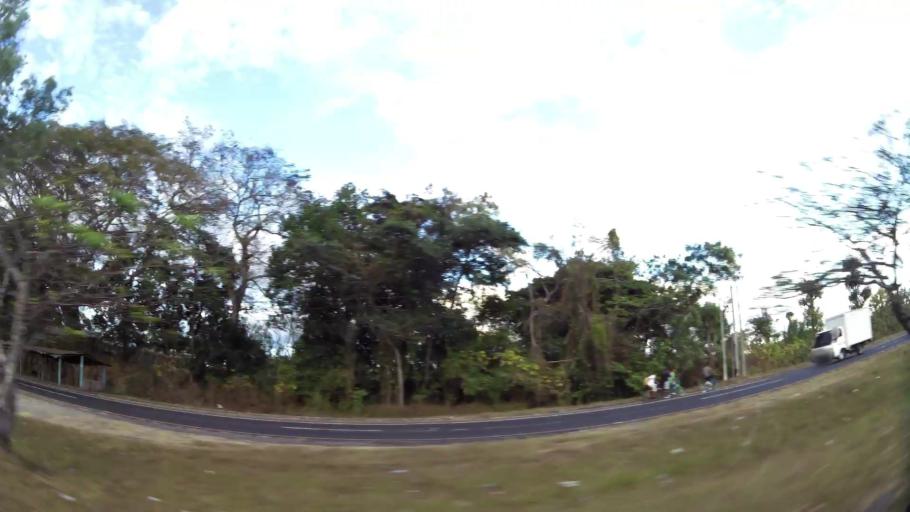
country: SV
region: San Vicente
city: San Sebastian
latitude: 13.7064
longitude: -88.8538
